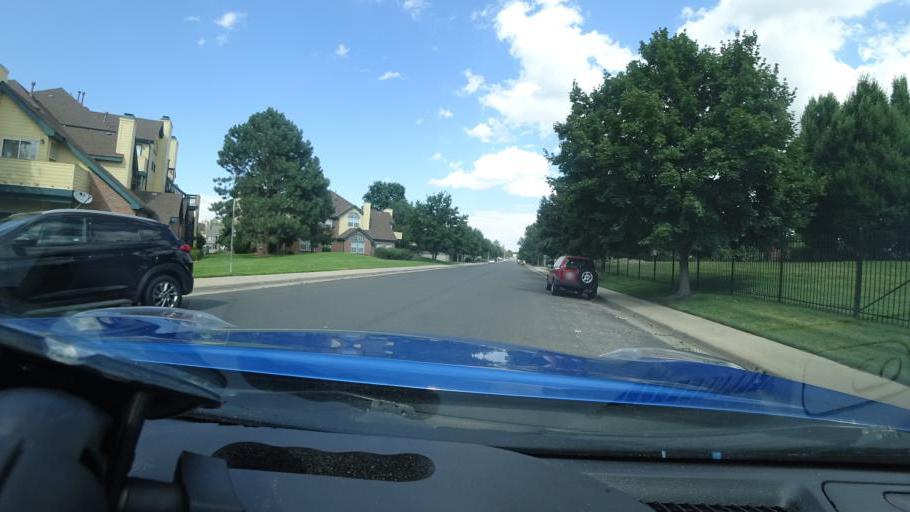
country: US
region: Colorado
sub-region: Adams County
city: Aurora
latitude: 39.6916
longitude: -104.8738
